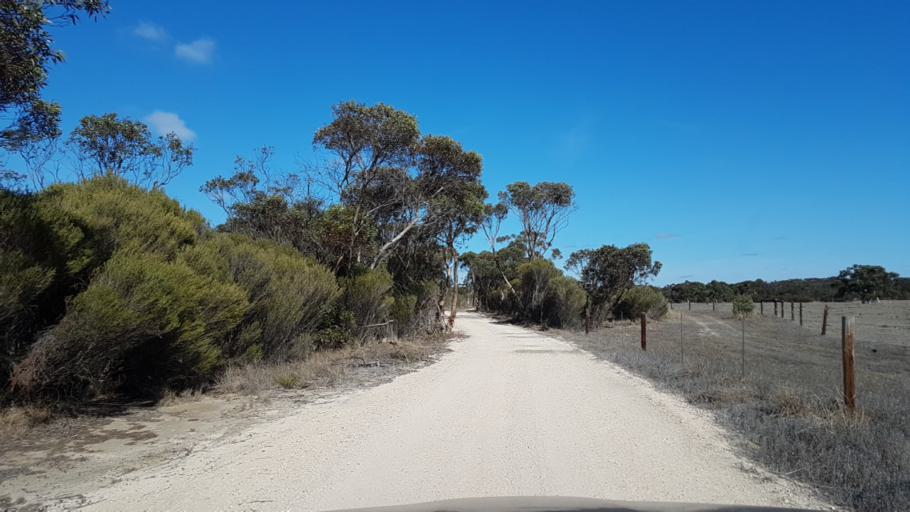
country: AU
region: South Australia
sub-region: Alexandrina
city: Strathalbyn
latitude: -35.3770
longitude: 138.8334
